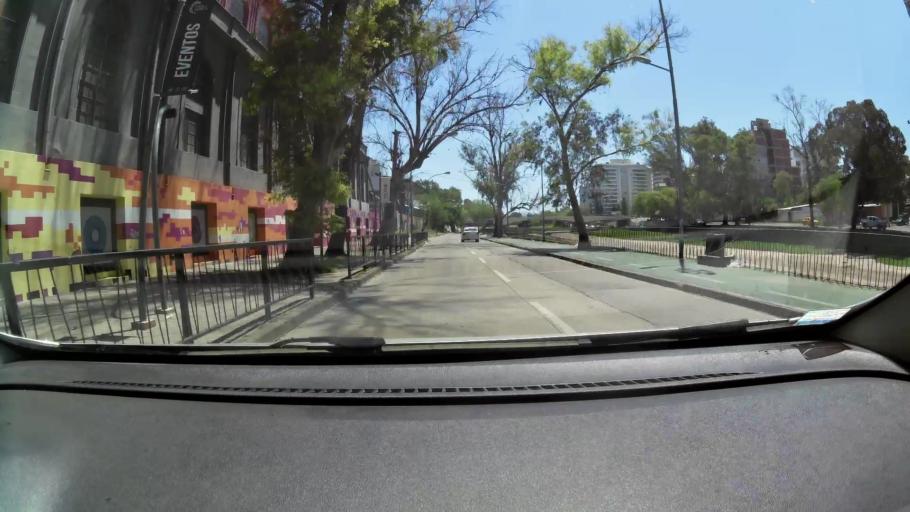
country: AR
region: Cordoba
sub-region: Departamento de Capital
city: Cordoba
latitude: -31.4057
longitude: -64.1974
